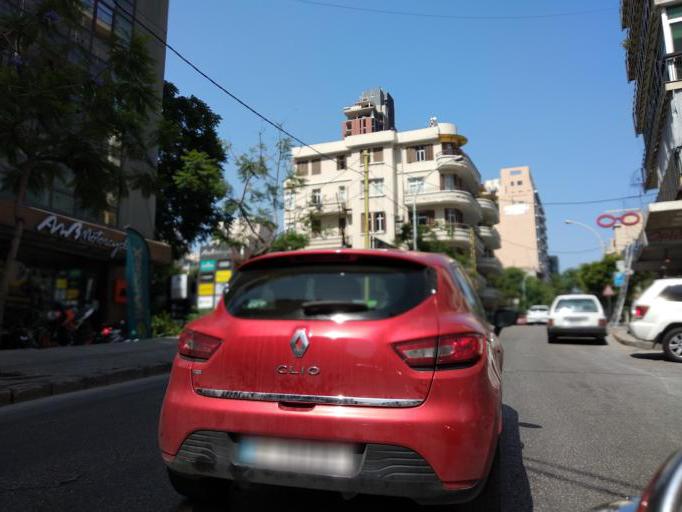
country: LB
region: Beyrouth
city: Beirut
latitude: 33.8955
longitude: 35.4938
